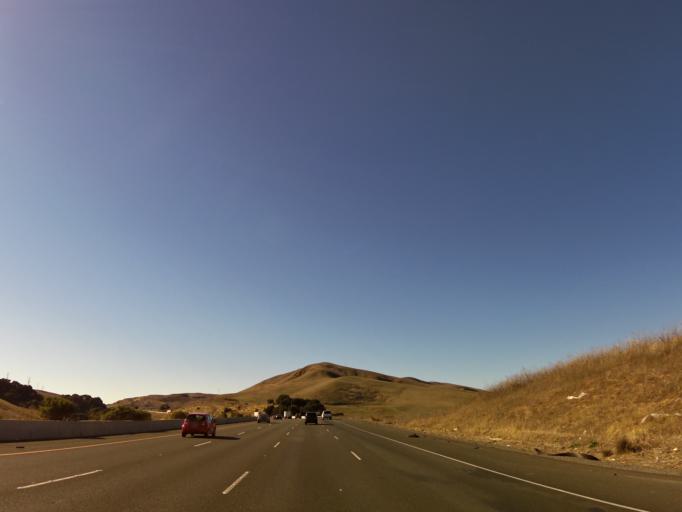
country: US
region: California
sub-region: Solano County
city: Green Valley
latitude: 38.1868
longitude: -122.1771
